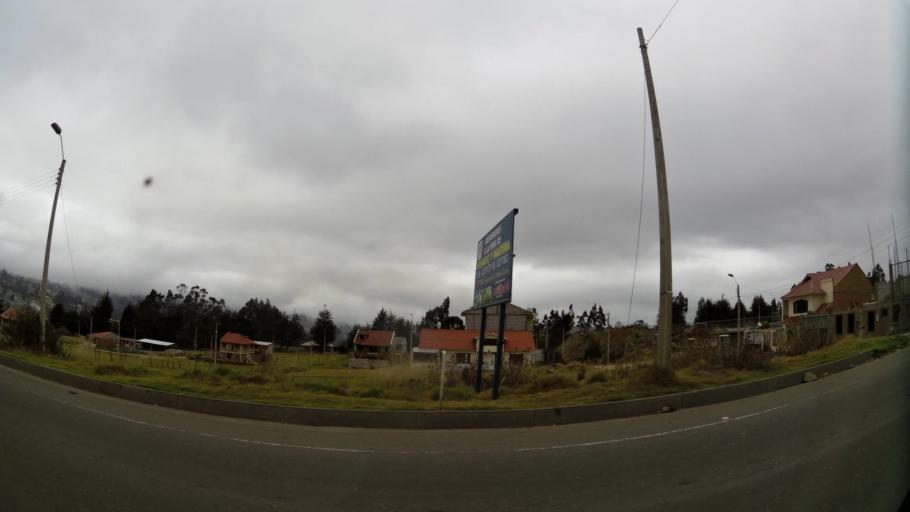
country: EC
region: Canar
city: Canar
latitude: -2.5211
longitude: -78.9274
